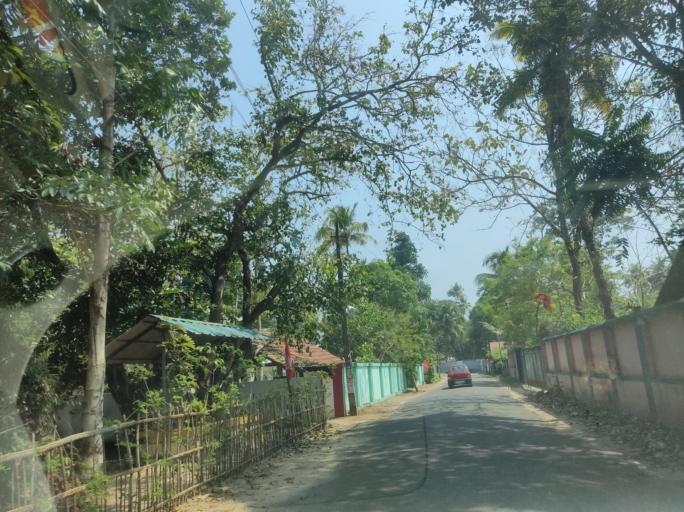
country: IN
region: Kerala
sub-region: Alappuzha
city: Vayalar
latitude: 9.6891
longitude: 76.3034
